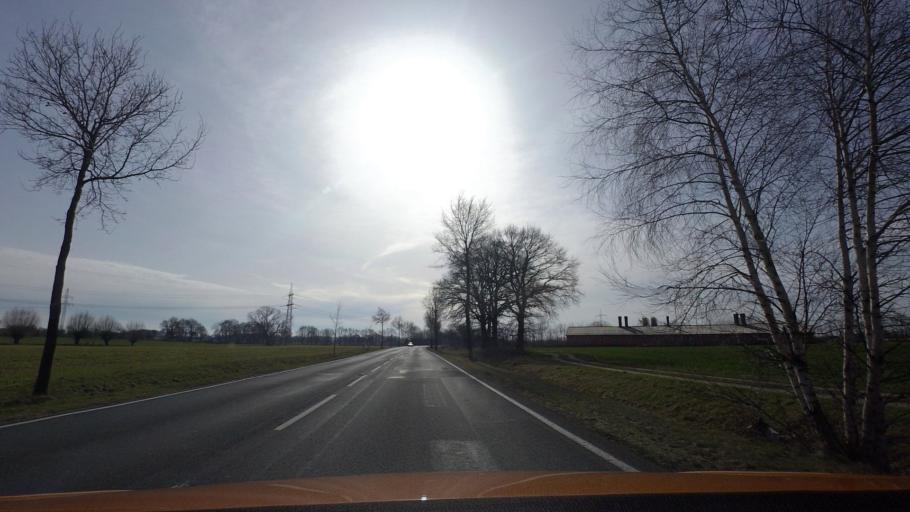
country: DE
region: Lower Saxony
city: Raddestorf
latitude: 52.4293
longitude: 8.9434
